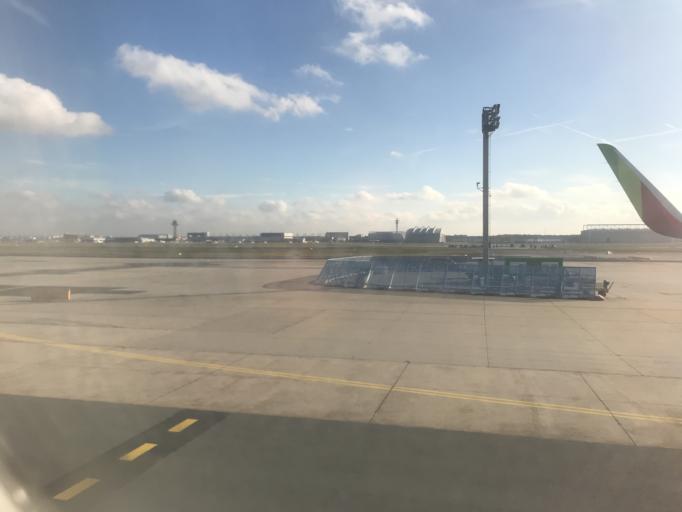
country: DE
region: Hesse
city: Kelsterbach
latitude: 50.0380
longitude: 8.5425
